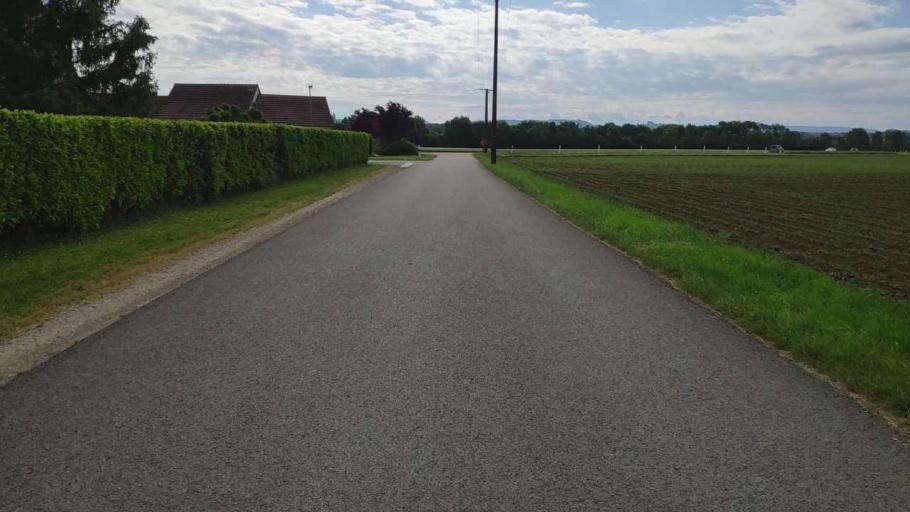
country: FR
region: Franche-Comte
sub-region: Departement du Jura
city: Bletterans
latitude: 46.7316
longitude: 5.4677
